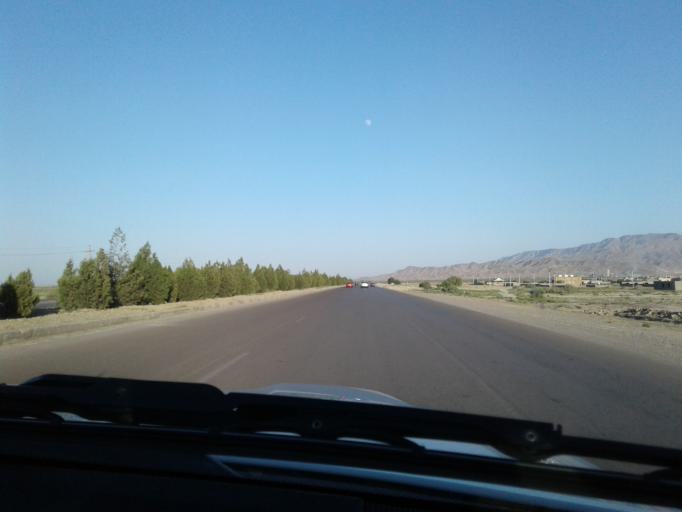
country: TM
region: Ahal
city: Baharly
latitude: 38.3076
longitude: 57.6188
